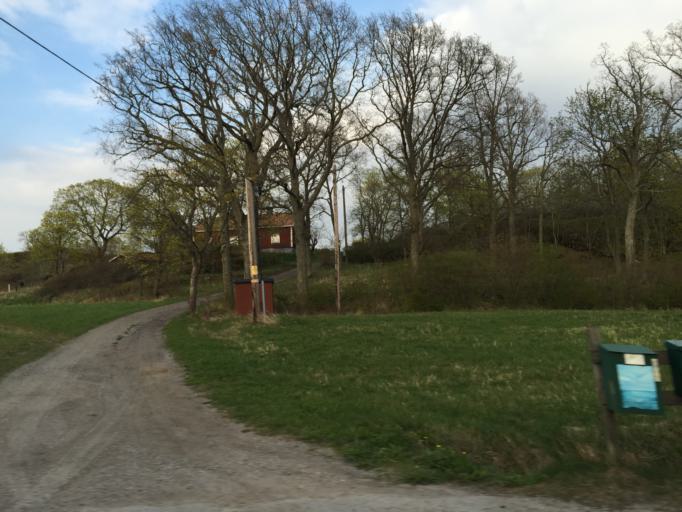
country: SE
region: Soedermanland
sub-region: Trosa Kommun
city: Vagnharad
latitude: 59.0140
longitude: 17.5947
